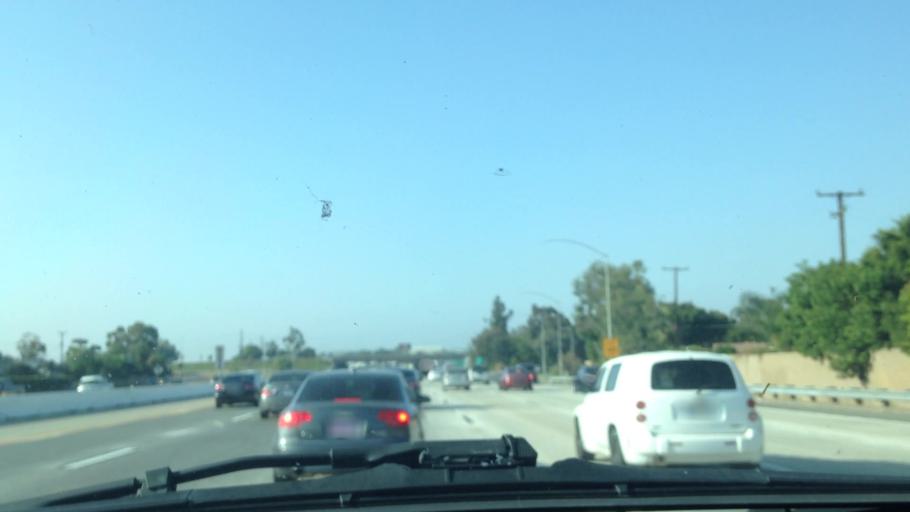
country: US
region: California
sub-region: Orange County
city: Anaheim
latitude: 33.8220
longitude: -117.8766
